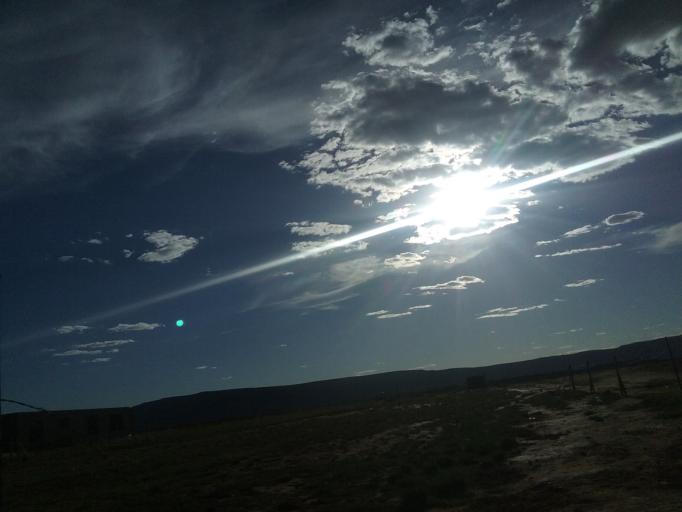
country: LS
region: Maseru
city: Maseru
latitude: -29.4259
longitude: 27.5686
